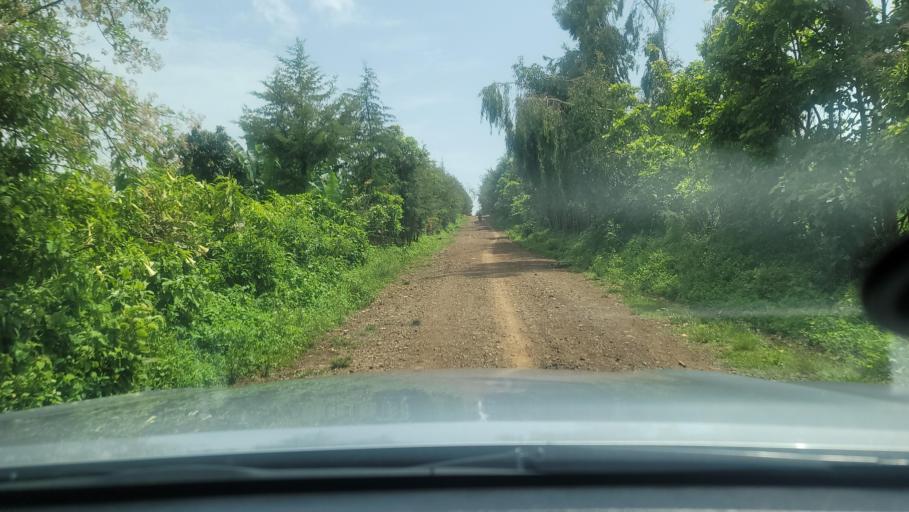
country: ET
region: Oromiya
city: Agaro
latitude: 7.8259
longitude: 36.4077
